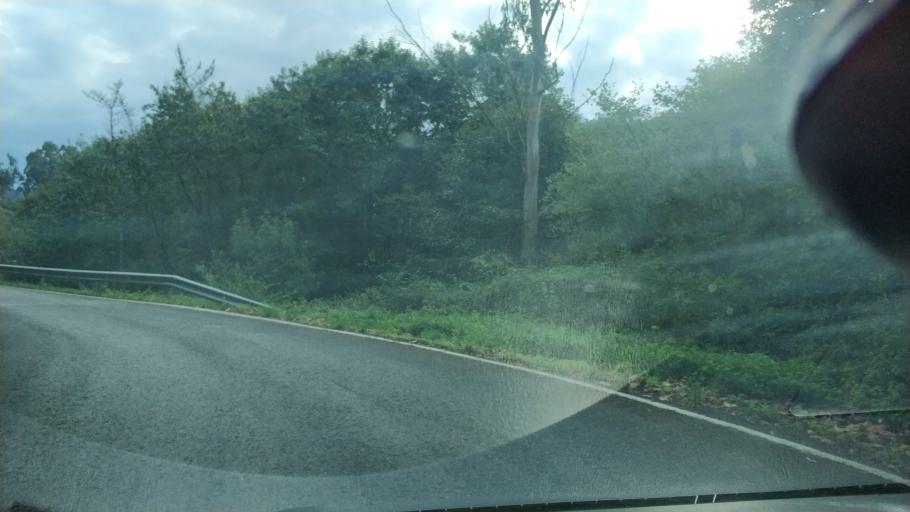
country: ES
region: Cantabria
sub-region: Provincia de Cantabria
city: Santa Maria de Cayon
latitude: 43.2885
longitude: -3.8309
